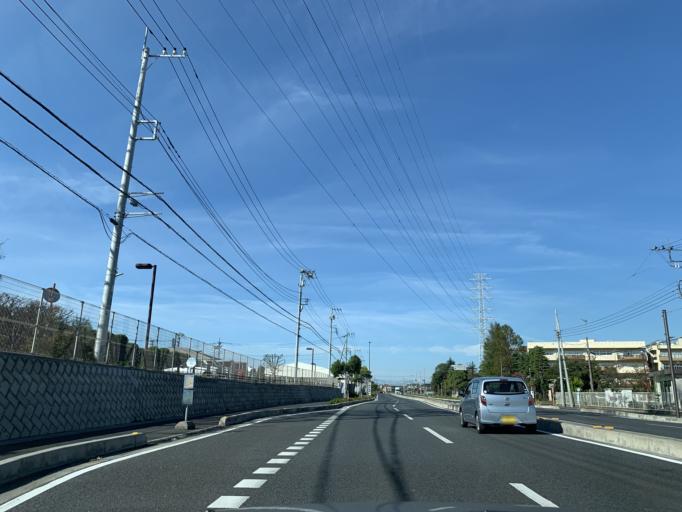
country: JP
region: Chiba
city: Nagareyama
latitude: 35.8355
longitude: 139.8742
